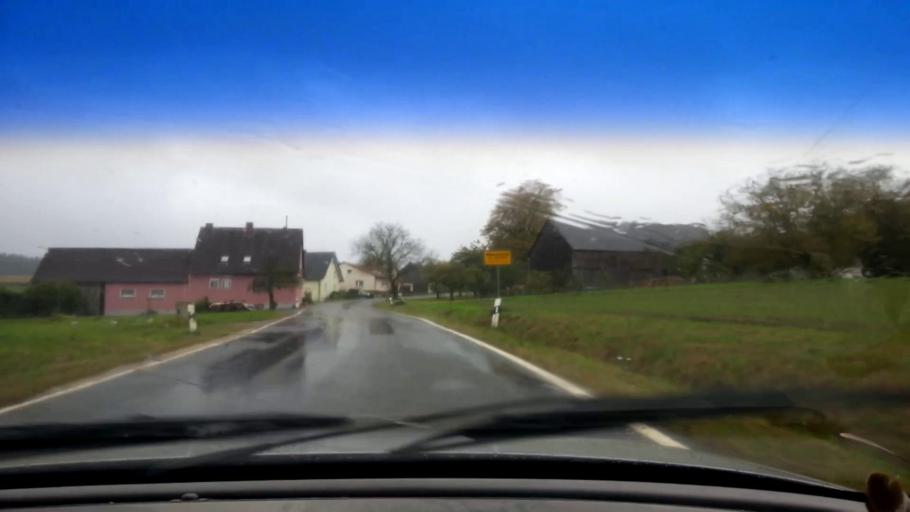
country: DE
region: Bavaria
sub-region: Upper Franconia
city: Wattendorf
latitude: 50.0375
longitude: 11.1551
